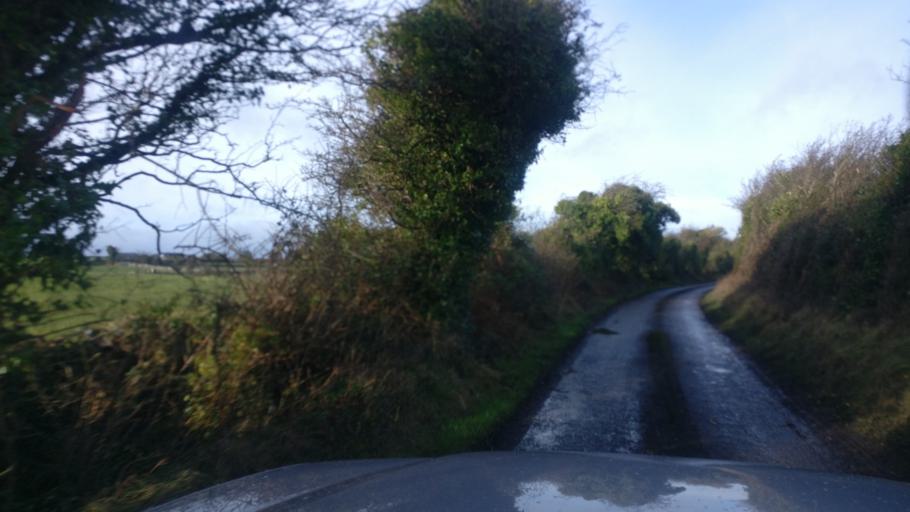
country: IE
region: Connaught
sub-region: County Galway
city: Loughrea
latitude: 53.2010
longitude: -8.6676
